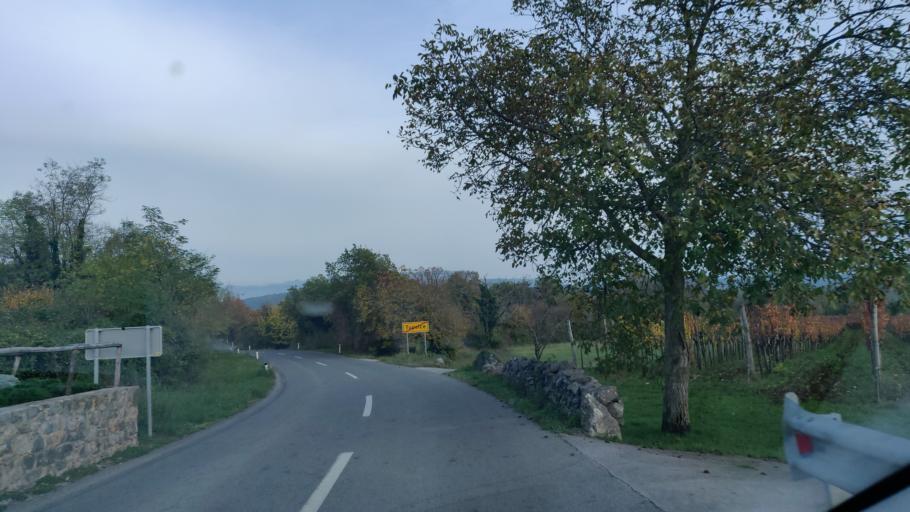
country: SI
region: Komen
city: Komen
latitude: 45.8144
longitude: 13.8157
